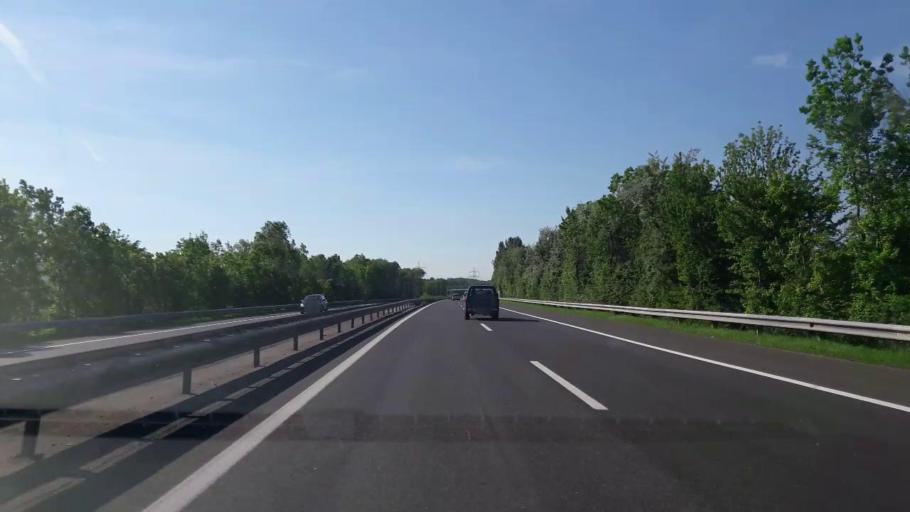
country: AT
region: Burgenland
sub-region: Eisenstadt-Umgebung
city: Wimpassing an der Leitha
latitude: 47.9127
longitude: 16.4084
